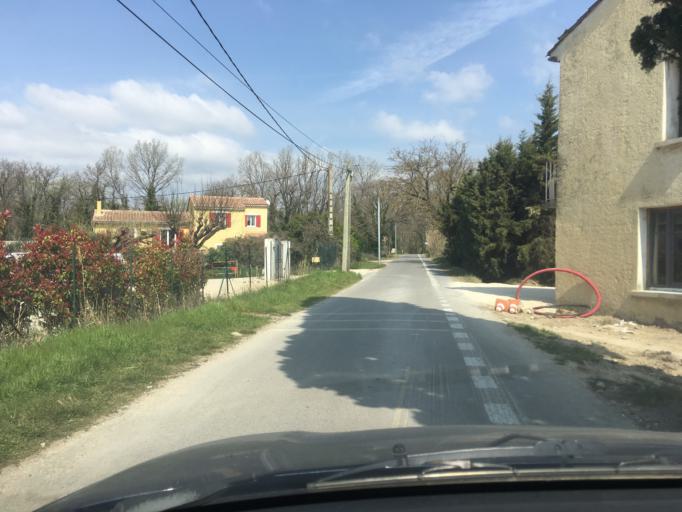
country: FR
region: Provence-Alpes-Cote d'Azur
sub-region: Departement du Vaucluse
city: Loriol-du-Comtat
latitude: 44.0855
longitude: 5.0095
